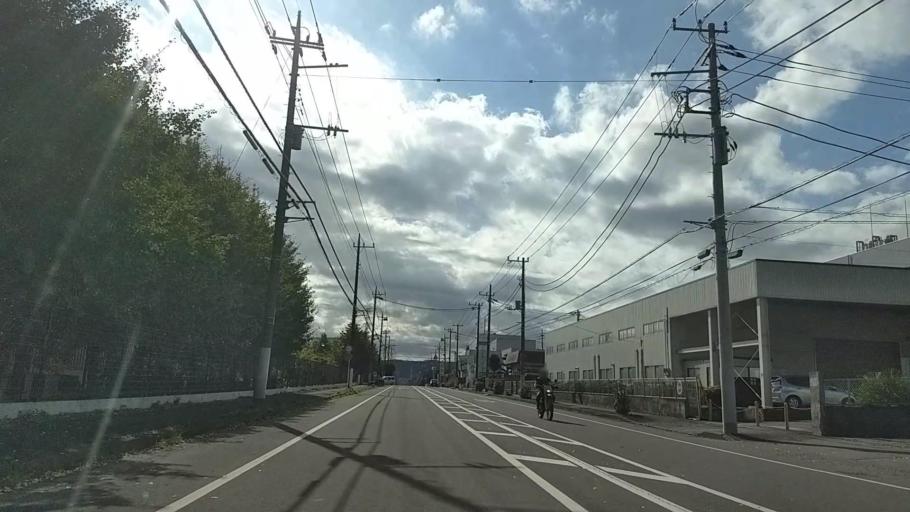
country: JP
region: Kanagawa
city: Hadano
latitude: 35.3883
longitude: 139.2033
